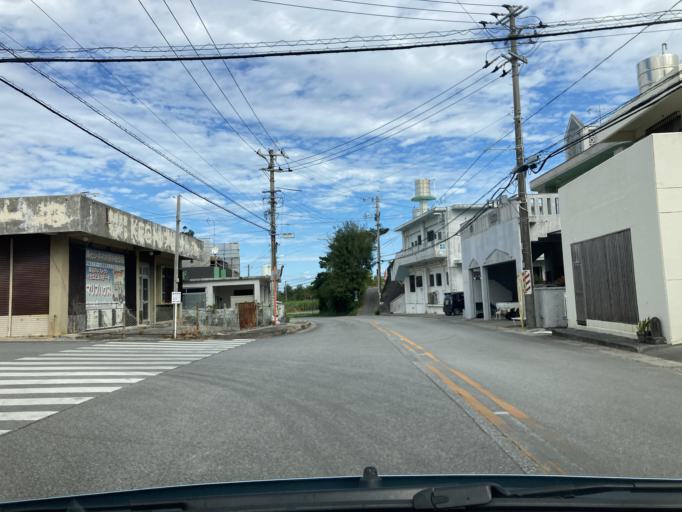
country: JP
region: Okinawa
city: Ishikawa
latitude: 26.4335
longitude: 127.7778
